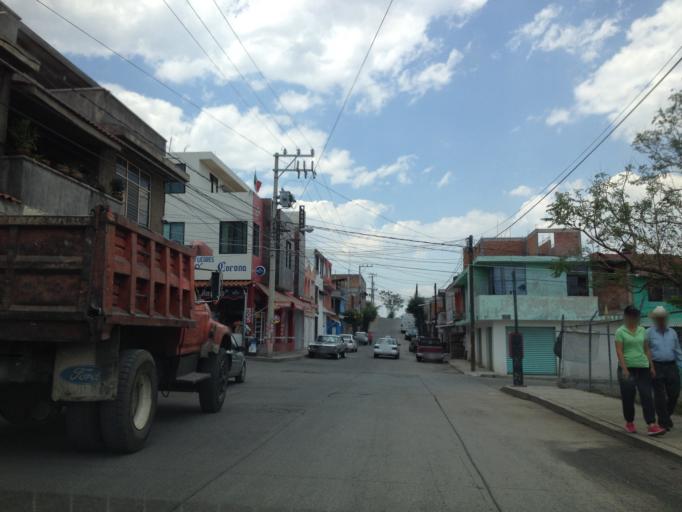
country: MX
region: Michoacan
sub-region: Morelia
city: San Antonio
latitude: 19.7038
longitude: -101.2474
